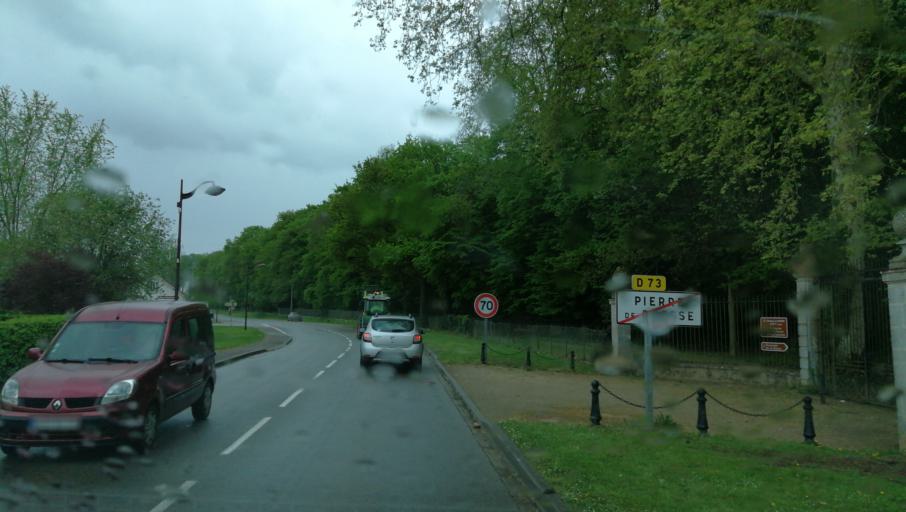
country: FR
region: Bourgogne
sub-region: Departement de Saone-et-Loire
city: Pierre-de-Bresse
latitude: 46.8825
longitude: 5.2678
